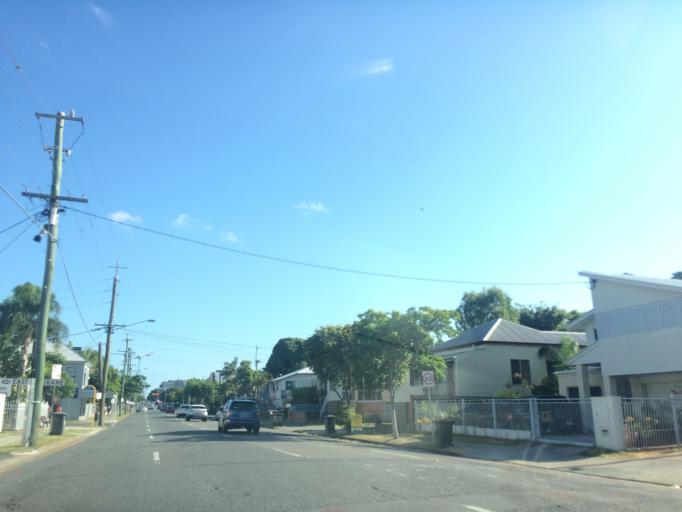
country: AU
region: Queensland
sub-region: Brisbane
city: Woolloongabba
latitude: -27.4850
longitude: 153.0402
